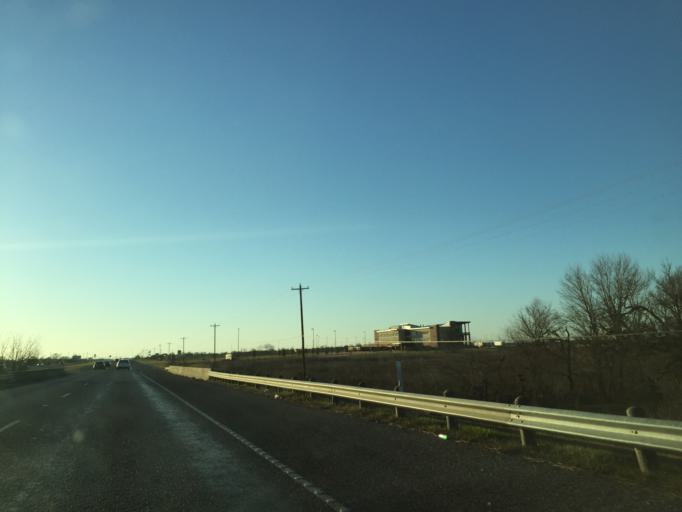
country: US
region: Texas
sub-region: Bastrop County
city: Elgin
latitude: 30.3522
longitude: -97.4020
